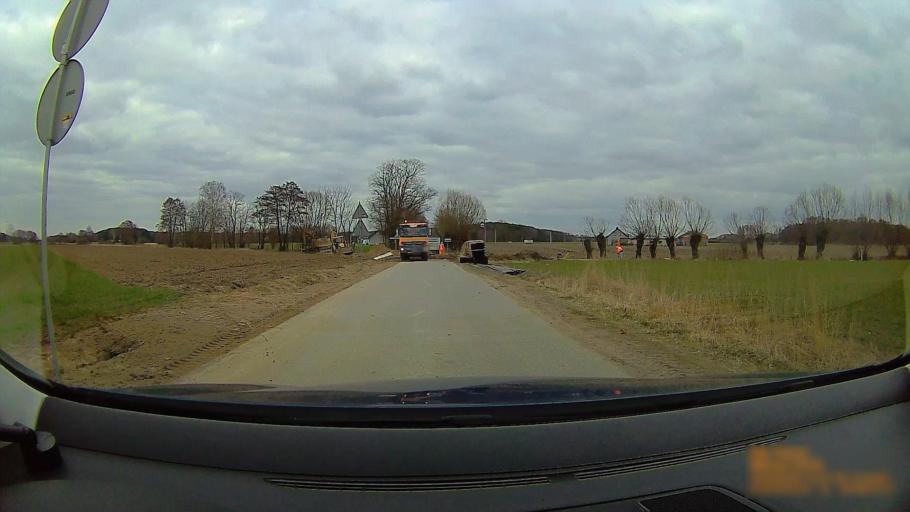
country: PL
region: Greater Poland Voivodeship
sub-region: Powiat koninski
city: Rzgow Pierwszy
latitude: 52.1288
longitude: 18.0714
